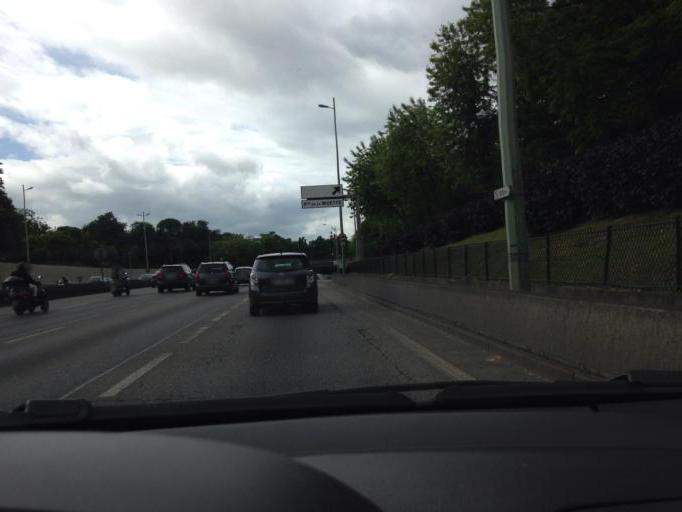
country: FR
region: Ile-de-France
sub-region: Departement des Hauts-de-Seine
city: Neuilly-sur-Seine
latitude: 48.8665
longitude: 2.2684
